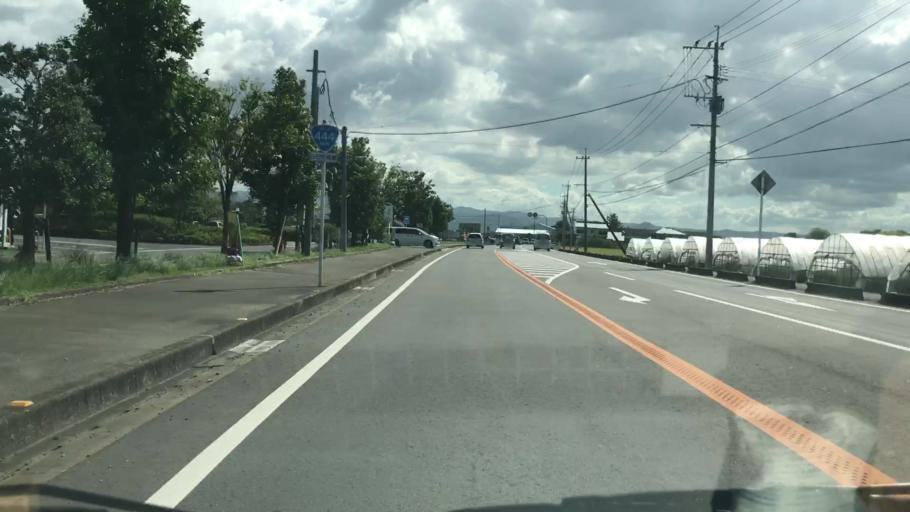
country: JP
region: Saga Prefecture
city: Kashima
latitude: 33.1812
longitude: 130.1893
